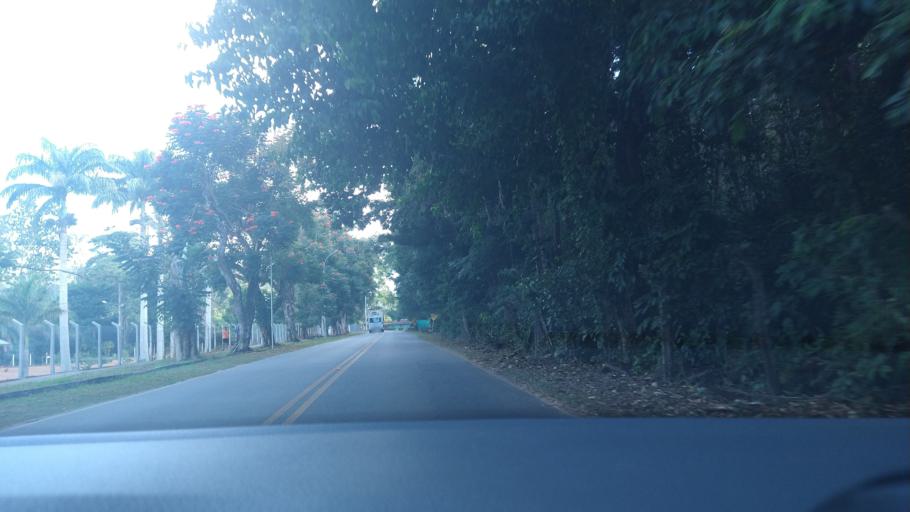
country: BR
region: Minas Gerais
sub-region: Vicosa
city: Vicosa
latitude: -20.7744
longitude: -42.8774
